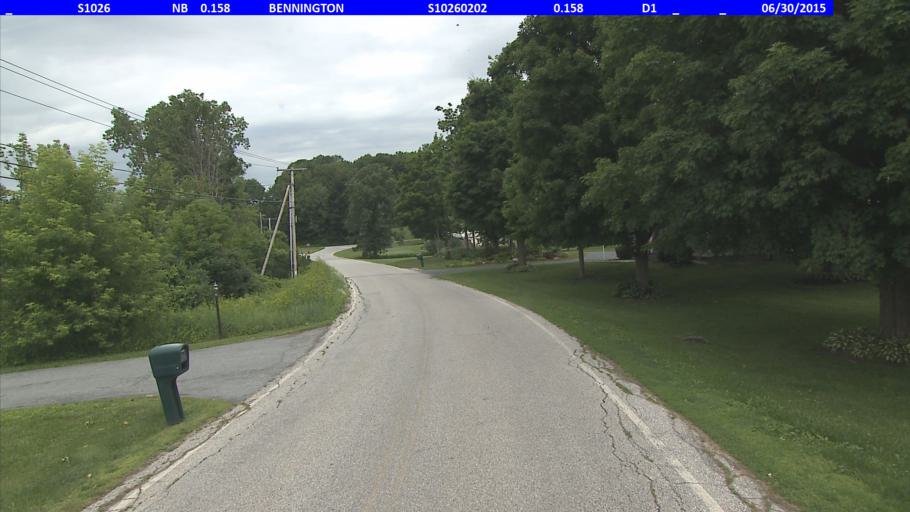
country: US
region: Vermont
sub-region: Bennington County
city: Bennington
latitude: 42.8845
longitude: -73.2285
